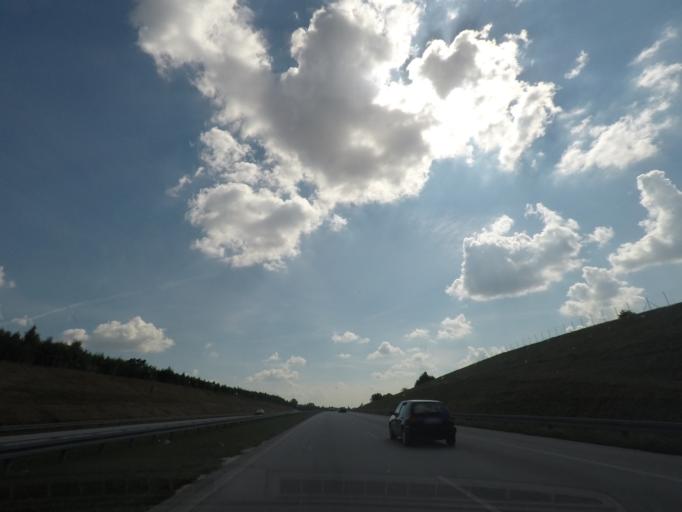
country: PL
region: Lodz Voivodeship
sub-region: Powiat zgierski
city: Strykow
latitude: 51.8313
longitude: 19.6542
